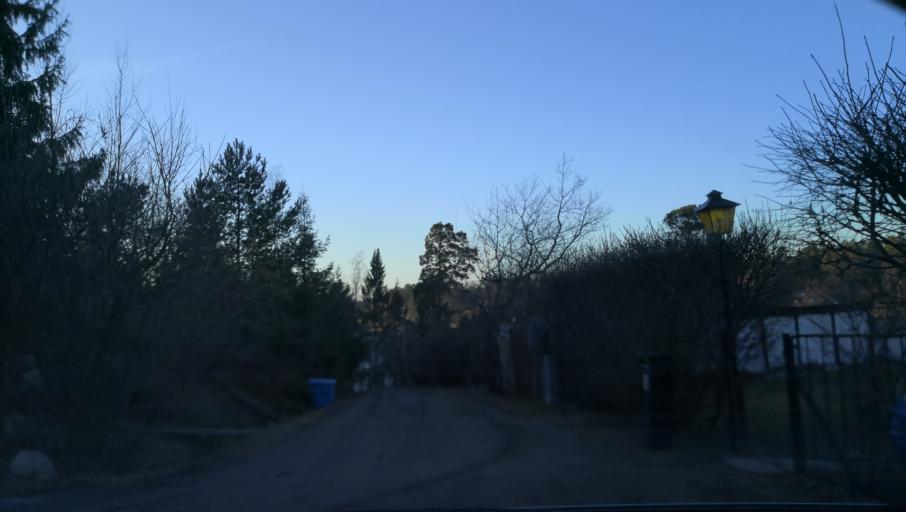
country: SE
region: Stockholm
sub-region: Varmdo Kommun
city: Mortnas
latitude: 59.3362
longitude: 18.4482
